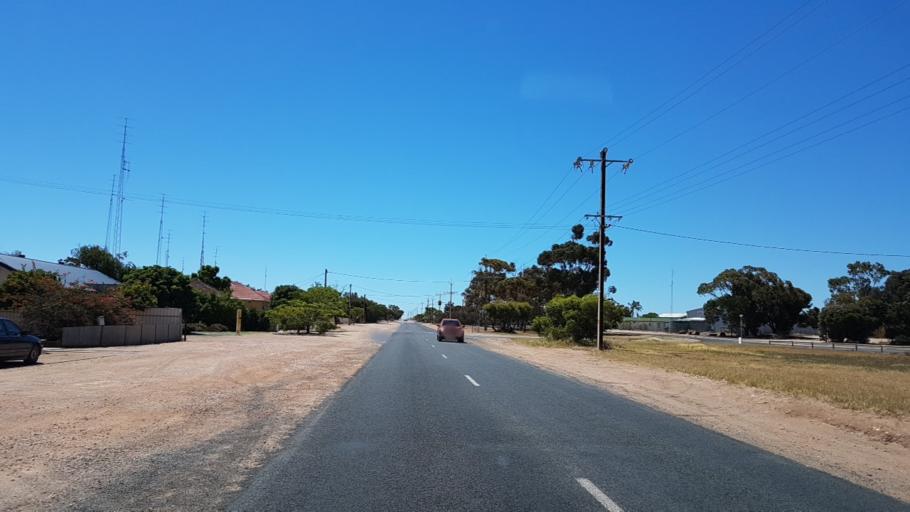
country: AU
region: South Australia
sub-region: Copper Coast
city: Wallaroo
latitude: -34.0558
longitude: 137.5930
